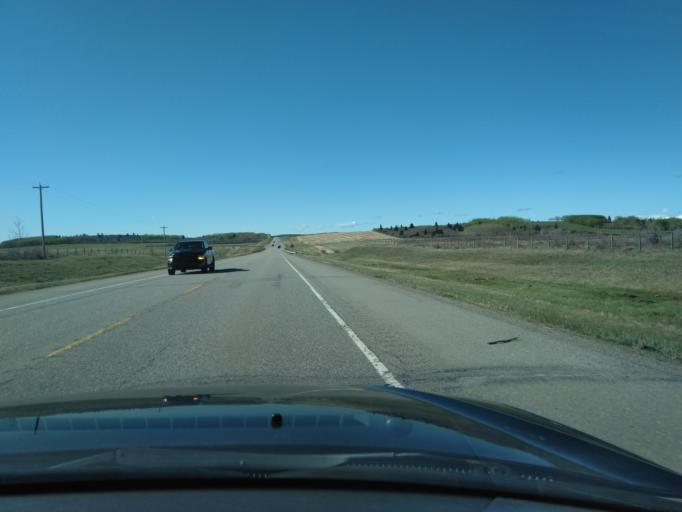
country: CA
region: Alberta
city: Cochrane
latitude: 51.0723
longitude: -114.4669
